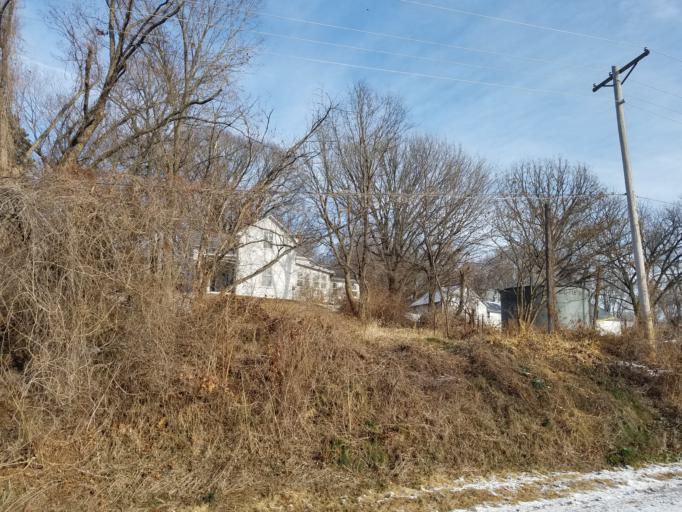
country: US
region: Missouri
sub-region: Ray County
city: Albany
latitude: 39.1314
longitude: -94.0274
